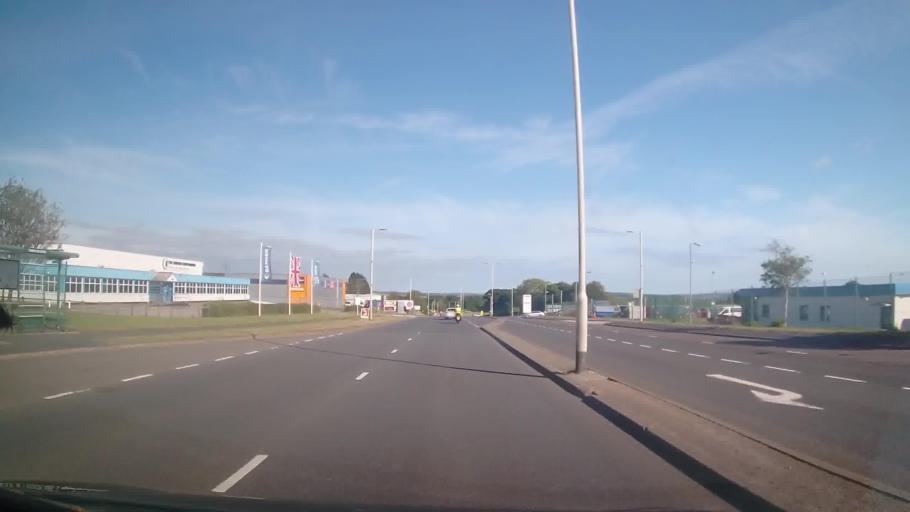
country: GB
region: England
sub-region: Devon
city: Plympton
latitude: 50.4197
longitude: -4.0935
